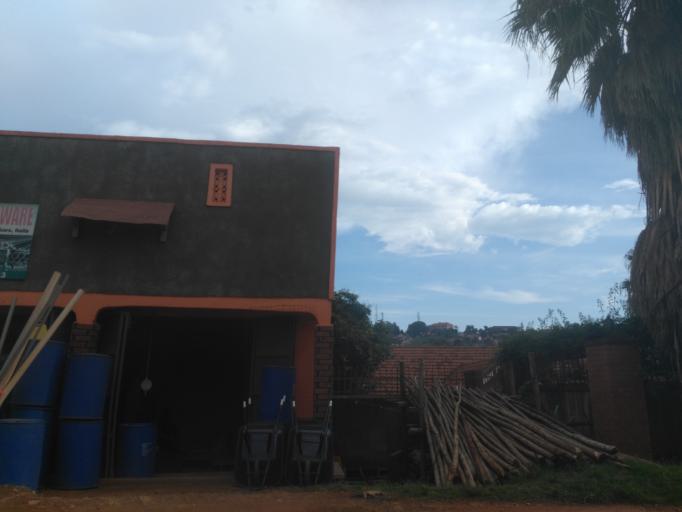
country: UG
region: Central Region
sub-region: Wakiso District
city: Kireka
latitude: 0.3689
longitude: 32.6124
